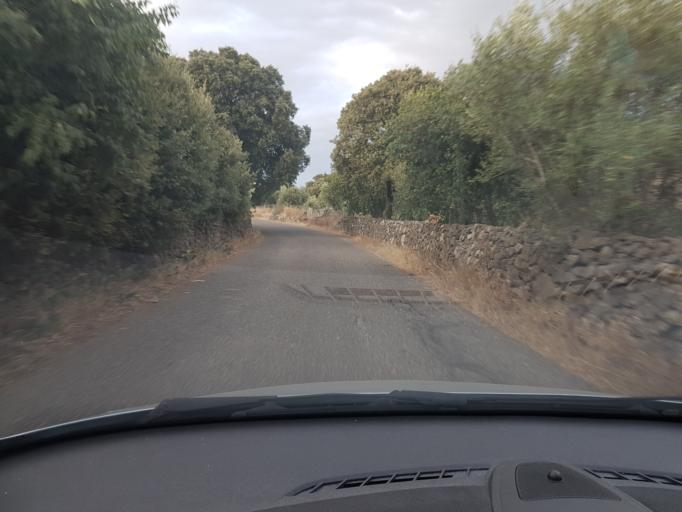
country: IT
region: Sardinia
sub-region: Provincia di Oristano
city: Seneghe
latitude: 40.0868
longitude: 8.6191
